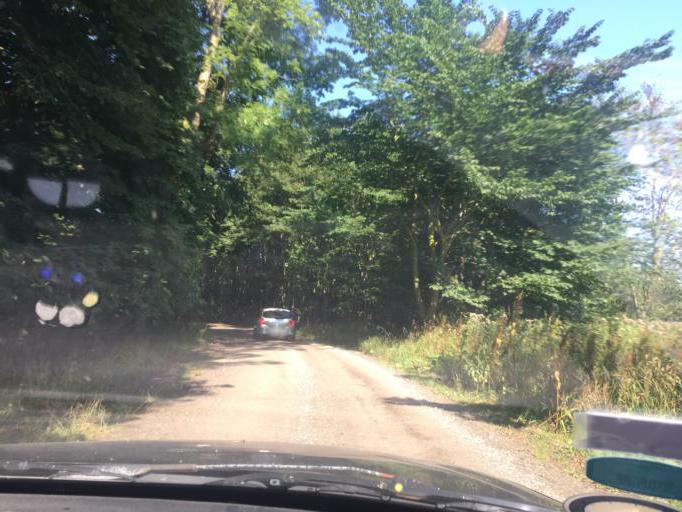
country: DK
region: Zealand
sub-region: Lolland Kommune
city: Maribo
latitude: 54.8155
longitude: 11.5039
